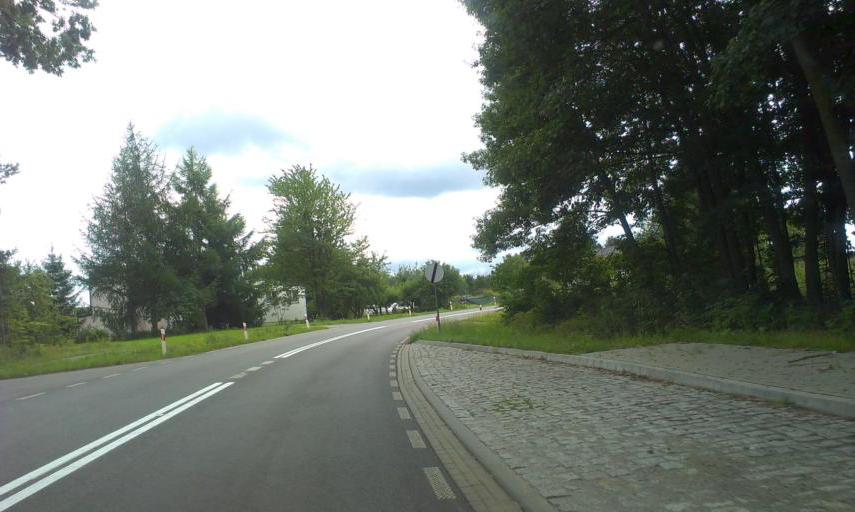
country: PL
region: West Pomeranian Voivodeship
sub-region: Koszalin
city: Koszalin
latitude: 54.1092
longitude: 16.1707
